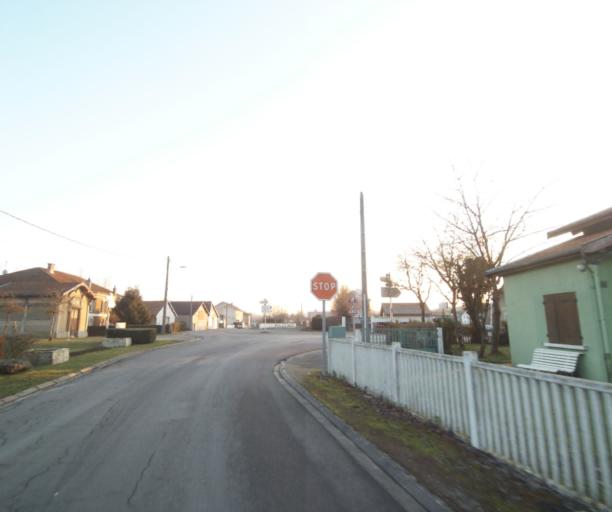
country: FR
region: Champagne-Ardenne
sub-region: Departement de la Haute-Marne
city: Bienville
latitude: 48.5838
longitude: 5.0451
